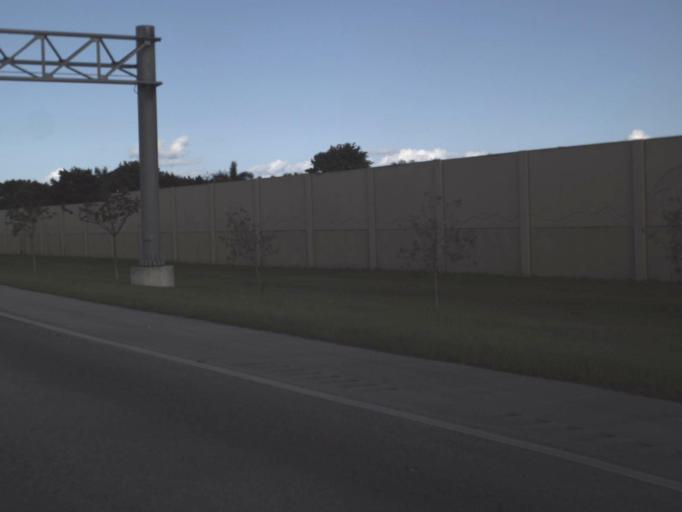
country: US
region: Florida
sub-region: Broward County
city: Palm Aire
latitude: 26.2252
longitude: -80.1826
